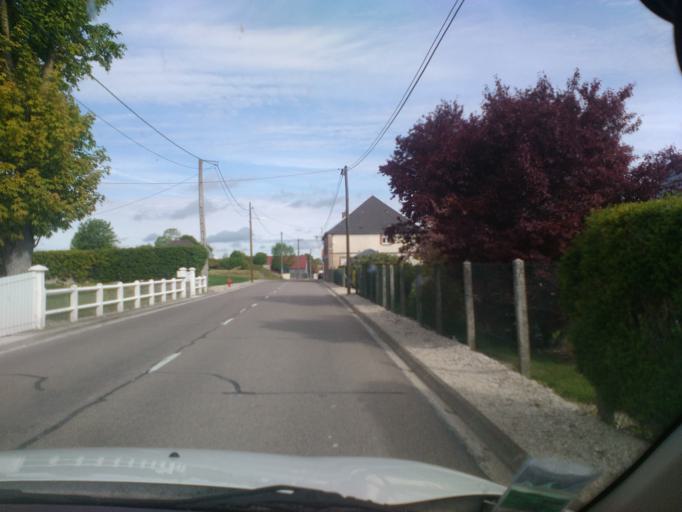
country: FR
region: Champagne-Ardenne
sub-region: Departement de l'Aube
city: Marigny-le-Chatel
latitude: 48.3868
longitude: 3.8336
